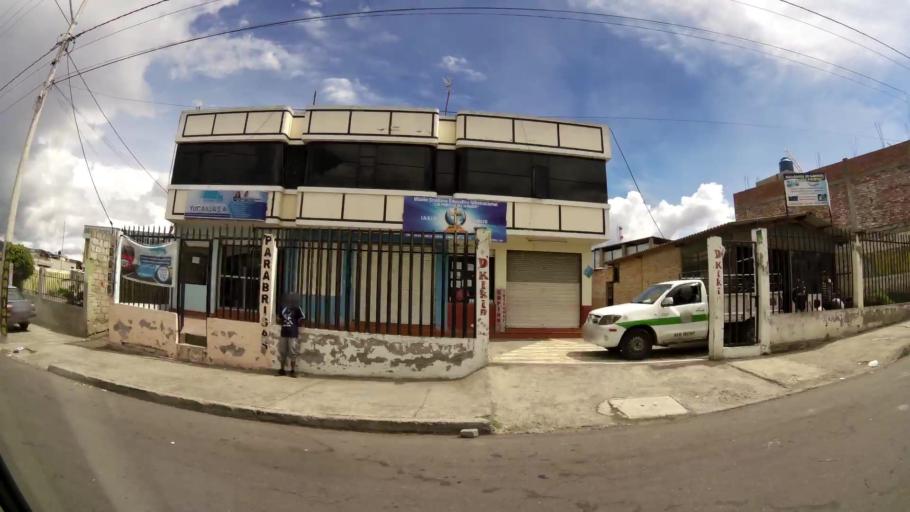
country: EC
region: Tungurahua
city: Ambato
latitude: -1.2705
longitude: -78.6186
